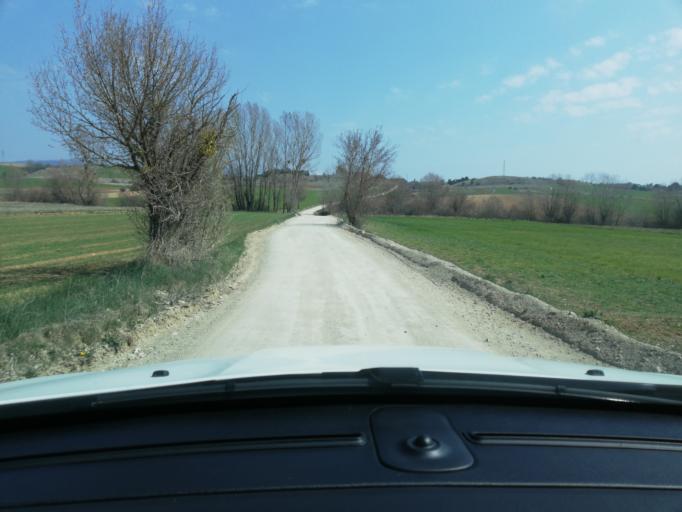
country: TR
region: Kastamonu
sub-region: Cide
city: Kastamonu
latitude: 41.4632
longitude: 33.7660
